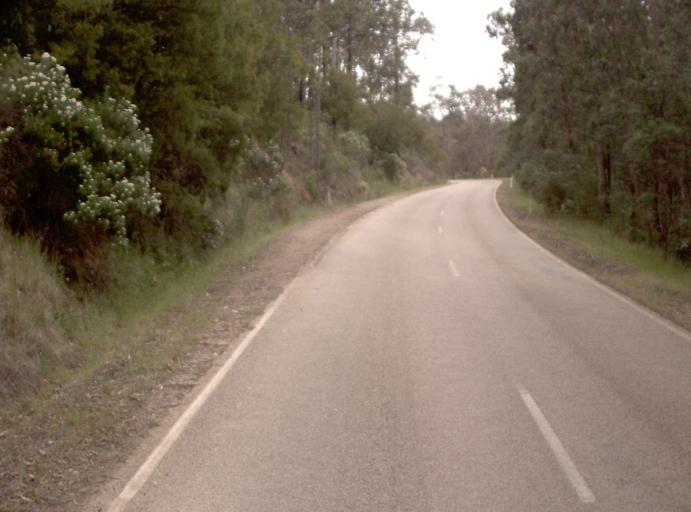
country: AU
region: Victoria
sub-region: East Gippsland
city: Bairnsdale
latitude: -37.6176
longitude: 147.1917
